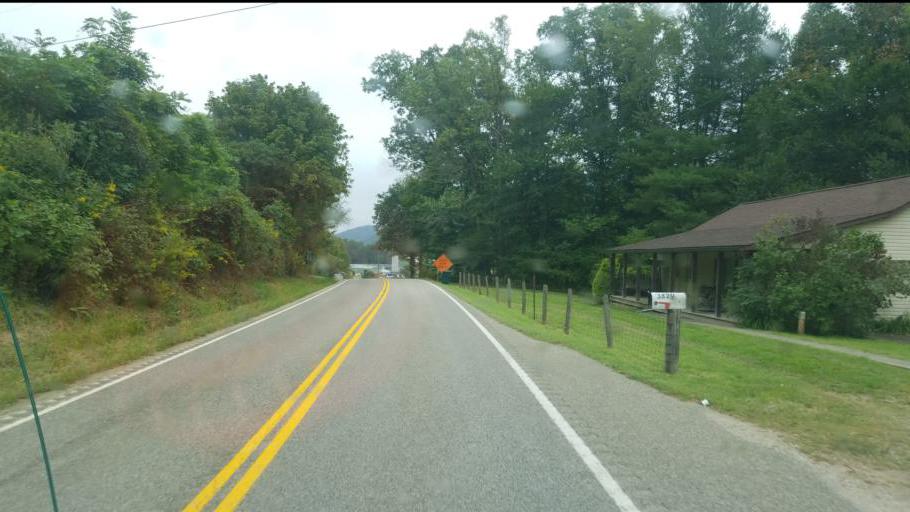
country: US
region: Kentucky
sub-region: Rowan County
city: Morehead
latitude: 38.2461
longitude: -83.4405
